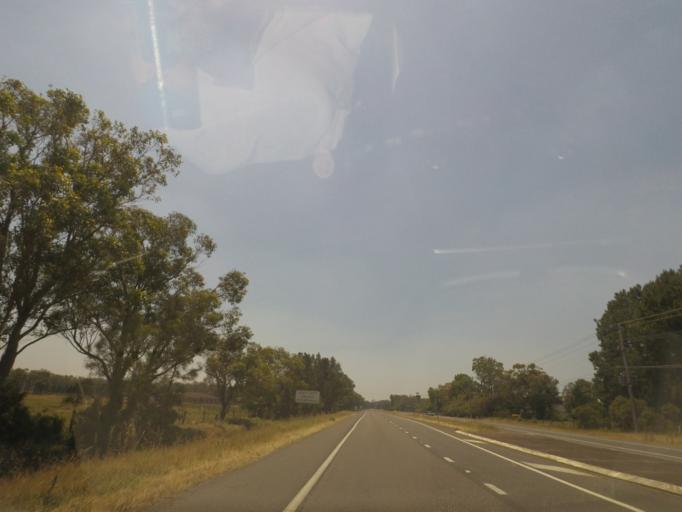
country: AU
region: New South Wales
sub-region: Port Stephens Shire
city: Medowie
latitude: -32.7936
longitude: 151.8961
